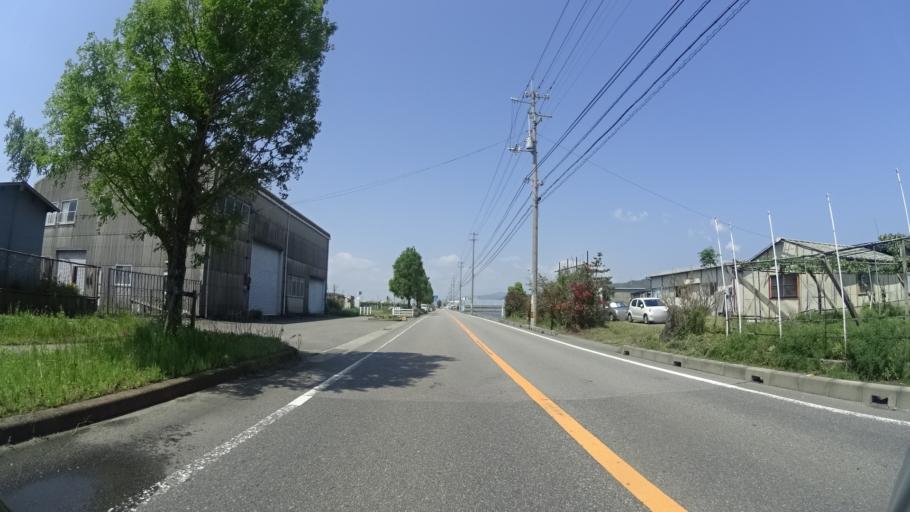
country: JP
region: Tokushima
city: Narutocho-mitsuishi
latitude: 34.1602
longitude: 134.5852
